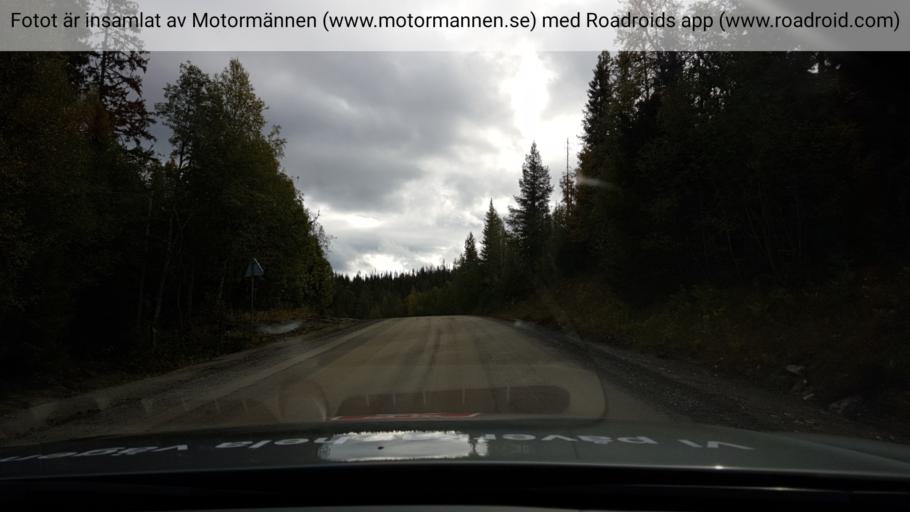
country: SE
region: Jaemtland
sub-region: Are Kommun
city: Are
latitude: 63.7185
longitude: 12.6091
